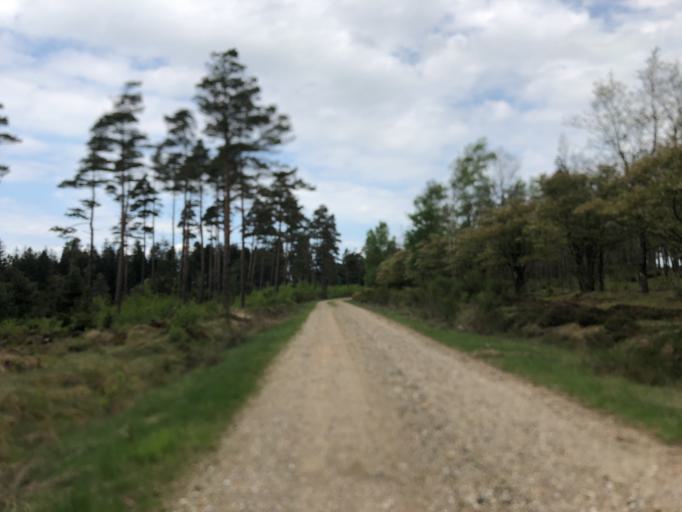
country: DK
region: Central Jutland
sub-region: Holstebro Kommune
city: Ulfborg
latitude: 56.2799
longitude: 8.4334
